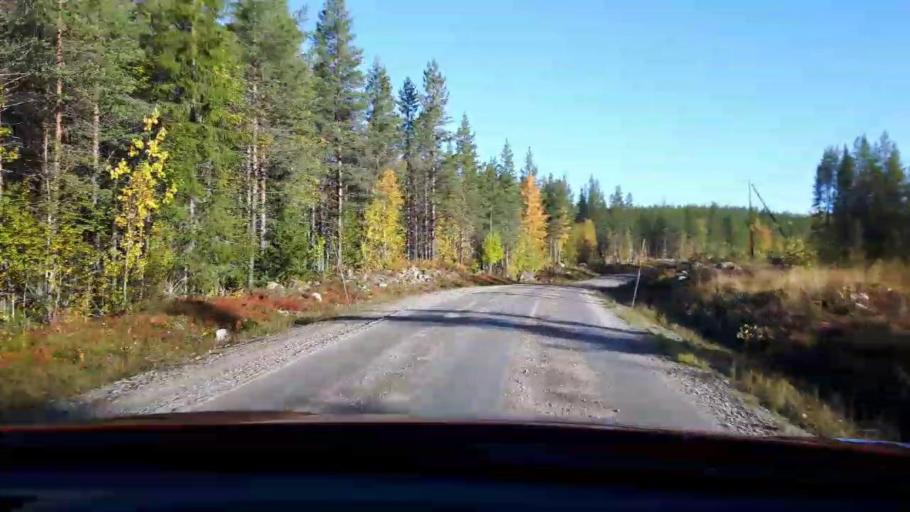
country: SE
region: Jaemtland
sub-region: Stroemsunds Kommun
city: Stroemsund
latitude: 64.3797
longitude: 15.1486
